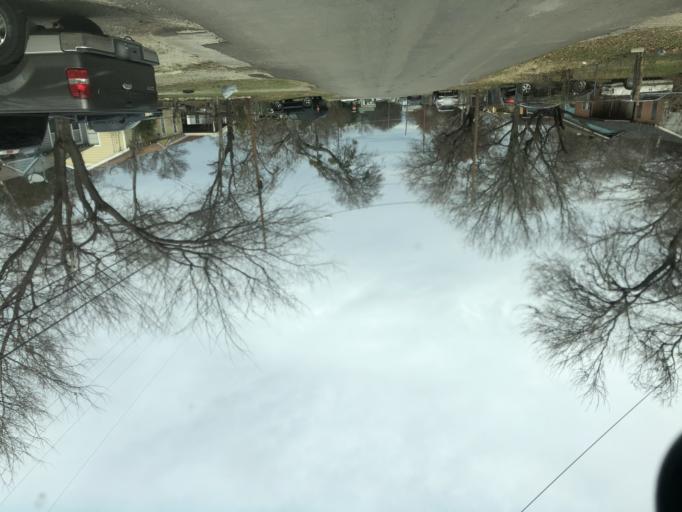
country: US
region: Texas
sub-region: Dallas County
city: Duncanville
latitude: 32.6677
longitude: -96.8325
